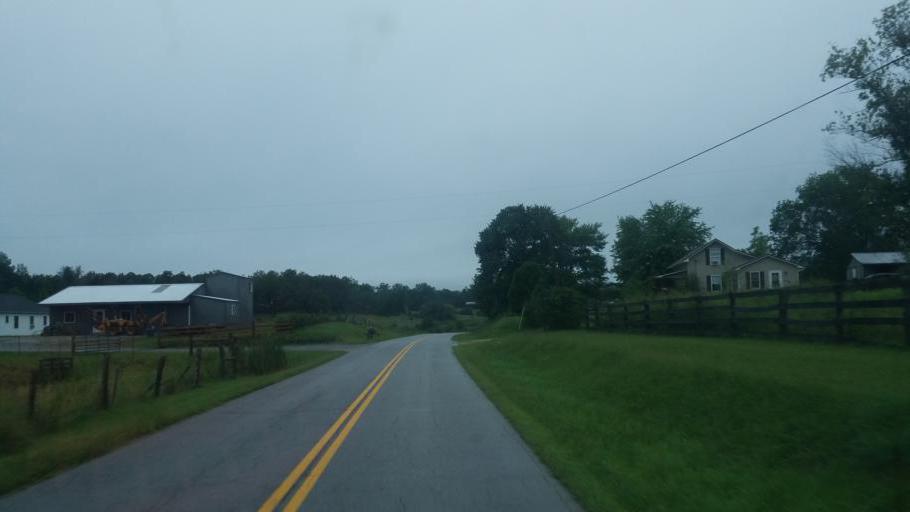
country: US
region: Kentucky
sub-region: Fleming County
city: Flemingsburg
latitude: 38.4035
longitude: -83.6183
